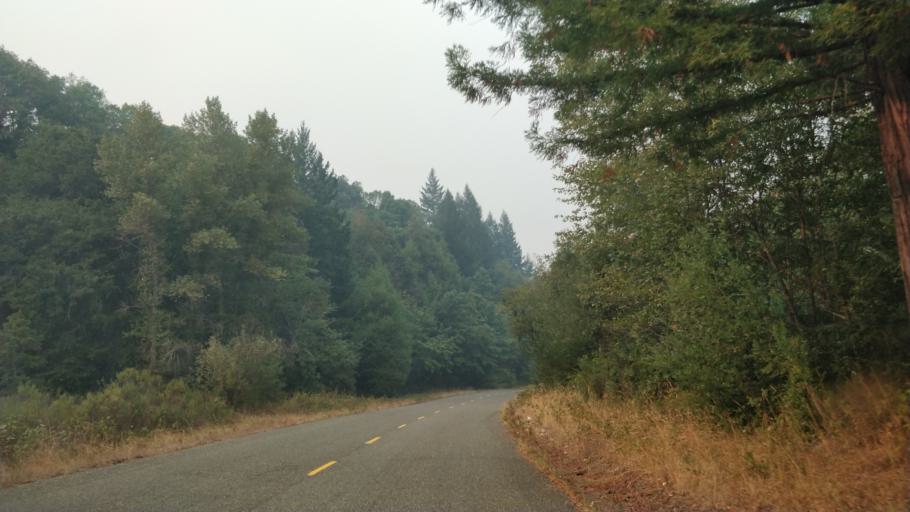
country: US
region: California
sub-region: Humboldt County
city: Rio Dell
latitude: 40.3380
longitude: -124.0274
